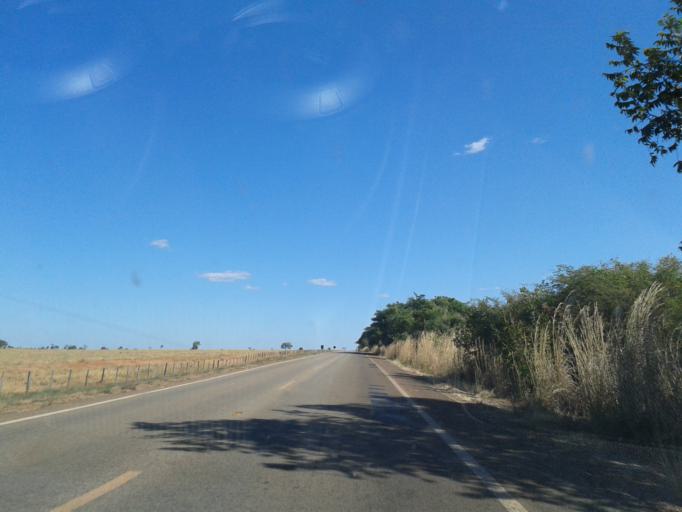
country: BR
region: Goias
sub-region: Mozarlandia
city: Mozarlandia
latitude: -14.3827
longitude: -50.4355
